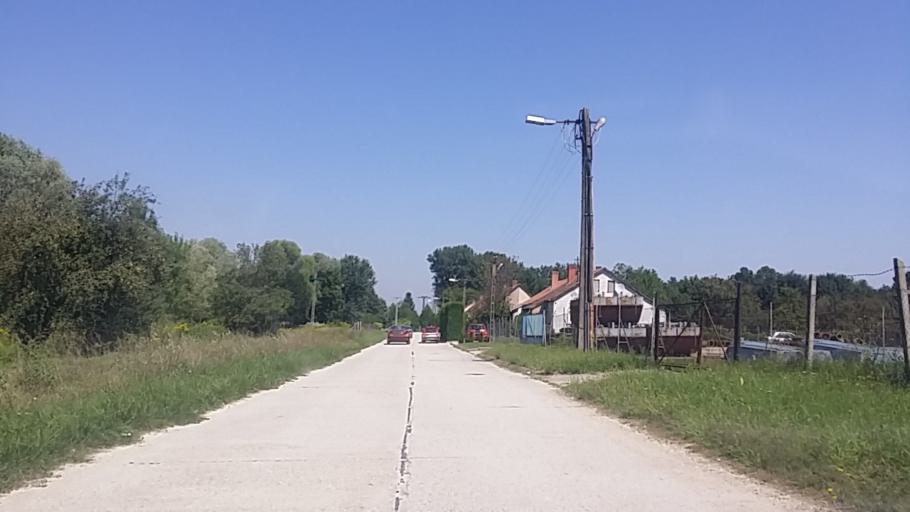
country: HU
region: Zala
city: Keszthely
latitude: 46.7018
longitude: 17.2381
